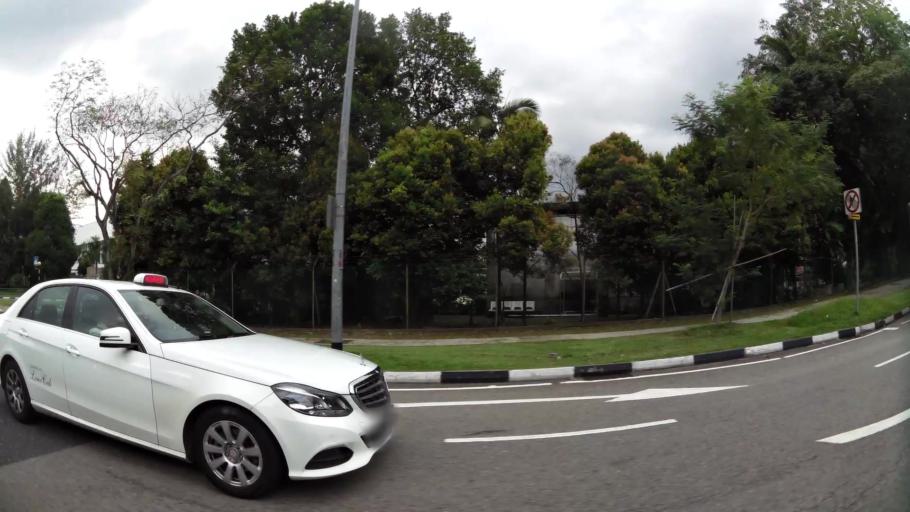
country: MY
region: Johor
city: Kampung Pasir Gudang Baru
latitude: 1.4588
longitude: 103.8233
